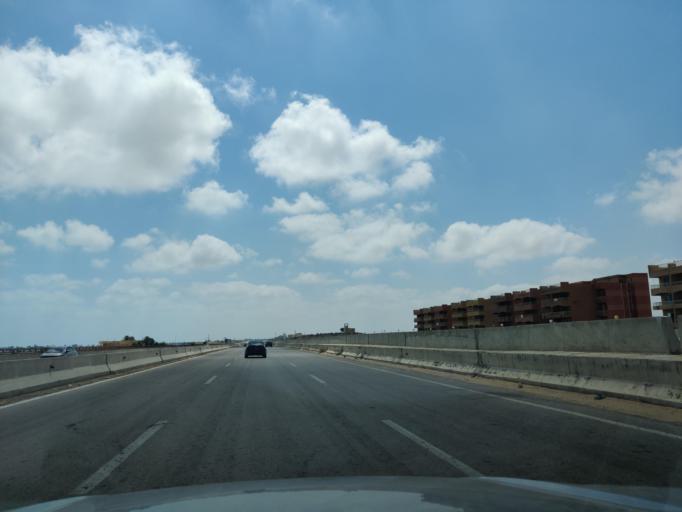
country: EG
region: Muhafazat Matruh
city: Al `Alamayn
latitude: 30.8219
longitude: 29.0017
